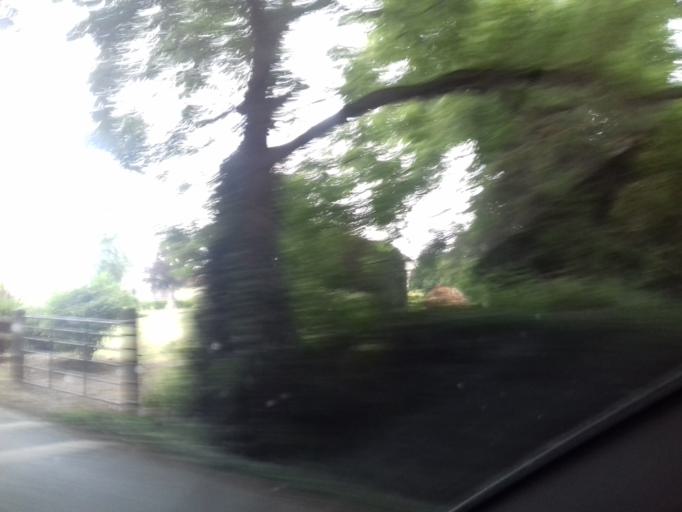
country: IE
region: Leinster
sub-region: Fingal County
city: Swords
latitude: 53.4883
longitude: -6.2654
